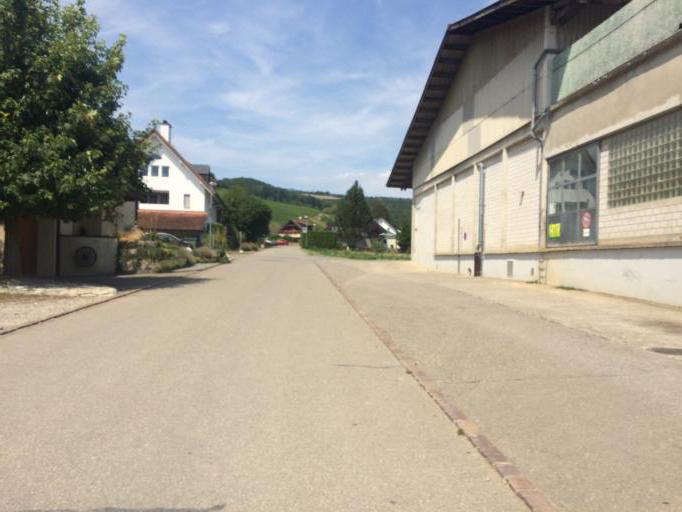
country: CH
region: Aargau
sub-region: Bezirk Brugg
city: Villigen
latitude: 47.5268
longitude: 8.2172
